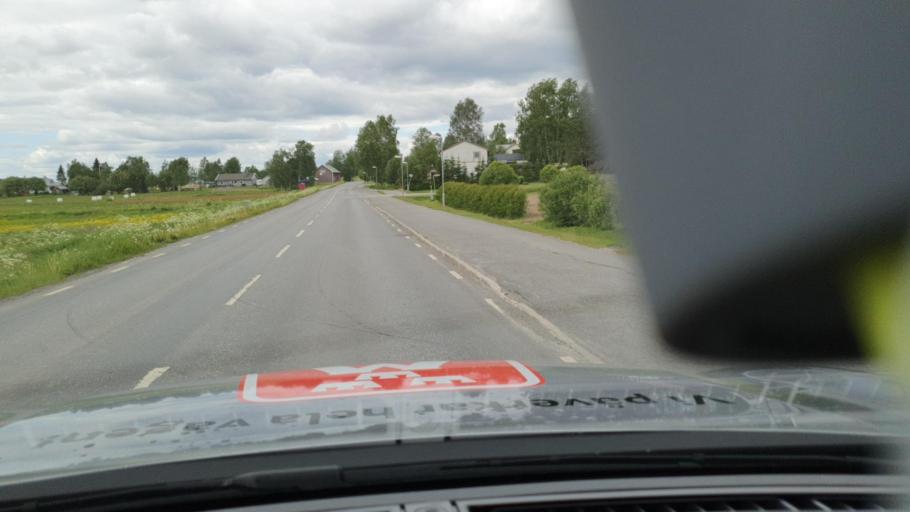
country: SE
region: Norrbotten
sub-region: Lulea Kommun
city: Gammelstad
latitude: 65.8080
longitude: 22.0238
